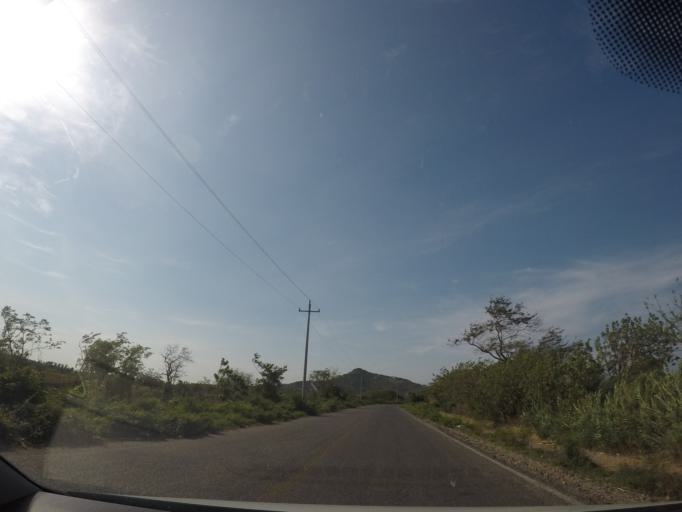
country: MX
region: Oaxaca
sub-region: Salina Cruz
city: Salina Cruz
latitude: 16.2239
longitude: -95.1353
